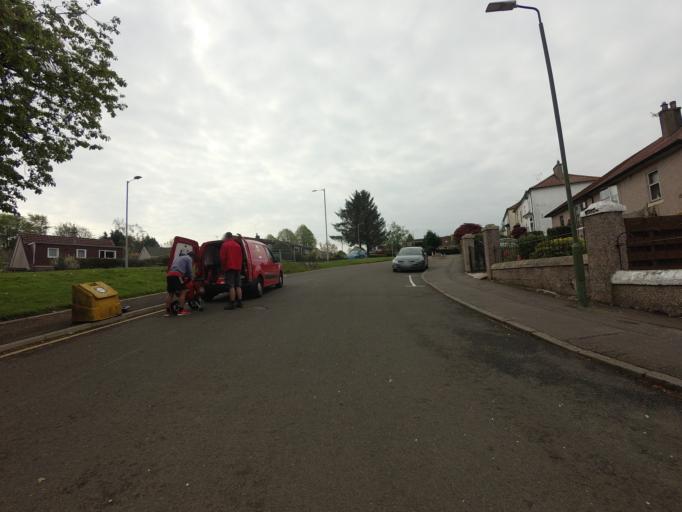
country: GB
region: Scotland
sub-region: Falkirk
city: Polmont
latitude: 55.9863
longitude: -3.7136
